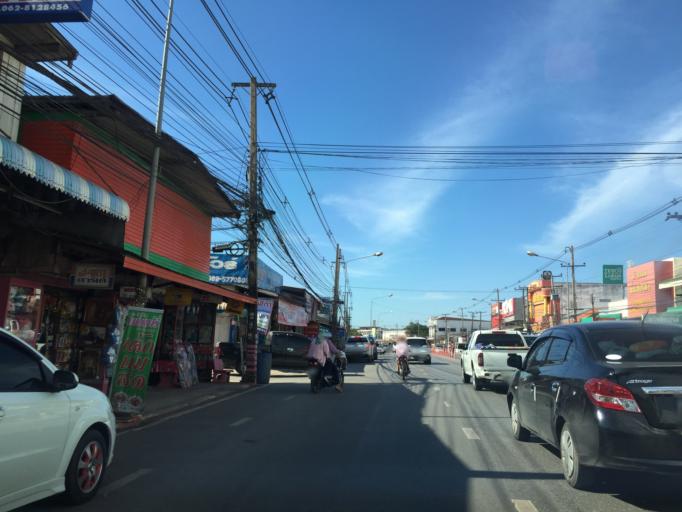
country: TH
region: Changwat Nong Bua Lamphu
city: Na Klang
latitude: 17.3013
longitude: 102.2049
